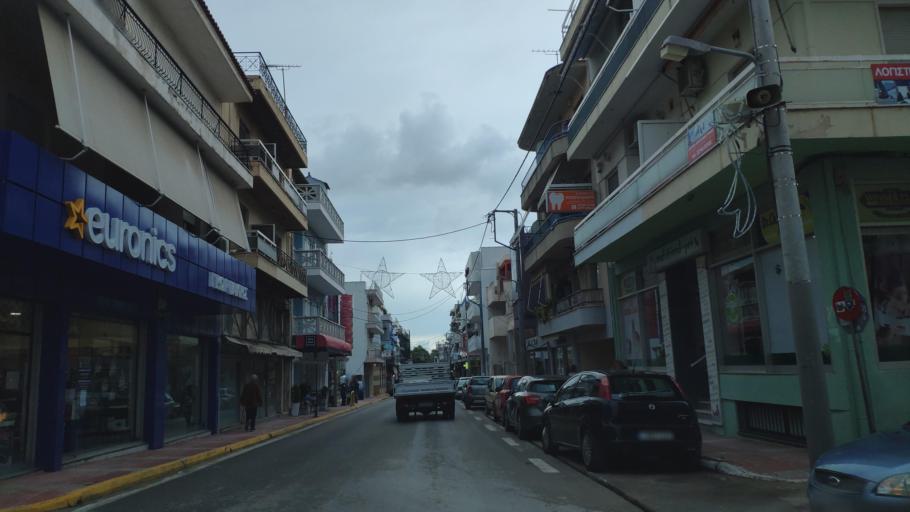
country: GR
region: Attica
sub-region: Nomarchia Anatolikis Attikis
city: Artemida
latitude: 37.9760
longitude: 24.0084
